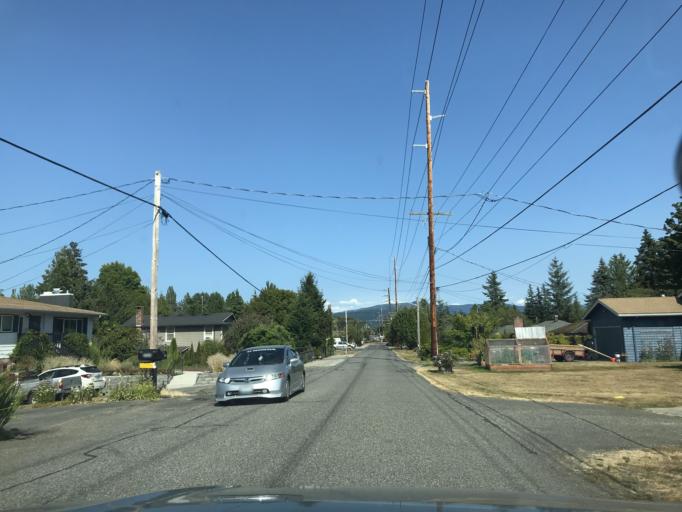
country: US
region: Washington
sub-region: Whatcom County
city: Bellingham
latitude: 48.7824
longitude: -122.5067
